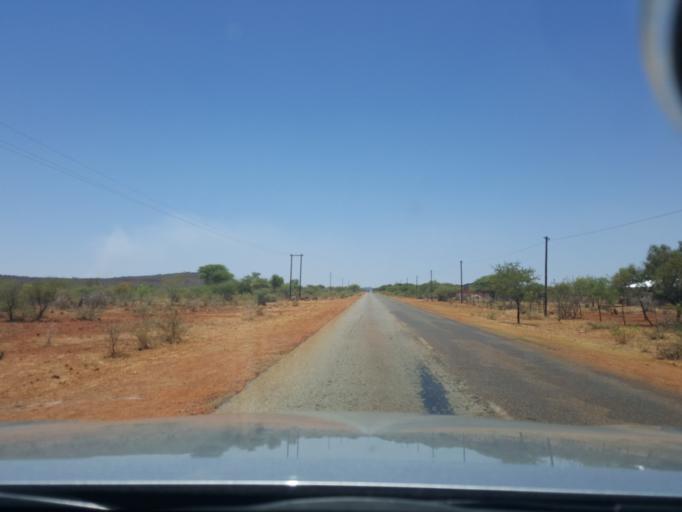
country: ZA
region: North-West
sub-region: Ngaka Modiri Molema District Municipality
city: Zeerust
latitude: -25.4038
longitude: 25.9438
